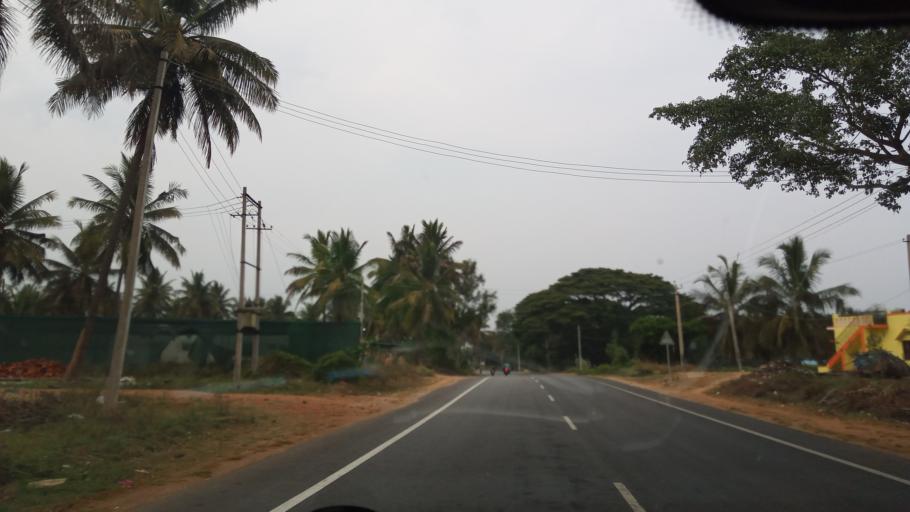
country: IN
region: Karnataka
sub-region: Mandya
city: Nagamangala
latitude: 12.7593
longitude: 76.7330
